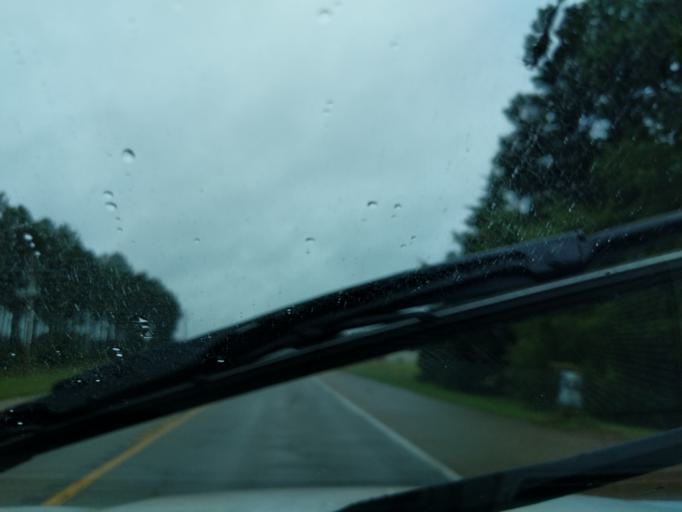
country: US
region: Louisiana
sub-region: Webster Parish
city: Minden
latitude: 32.5878
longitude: -93.2478
